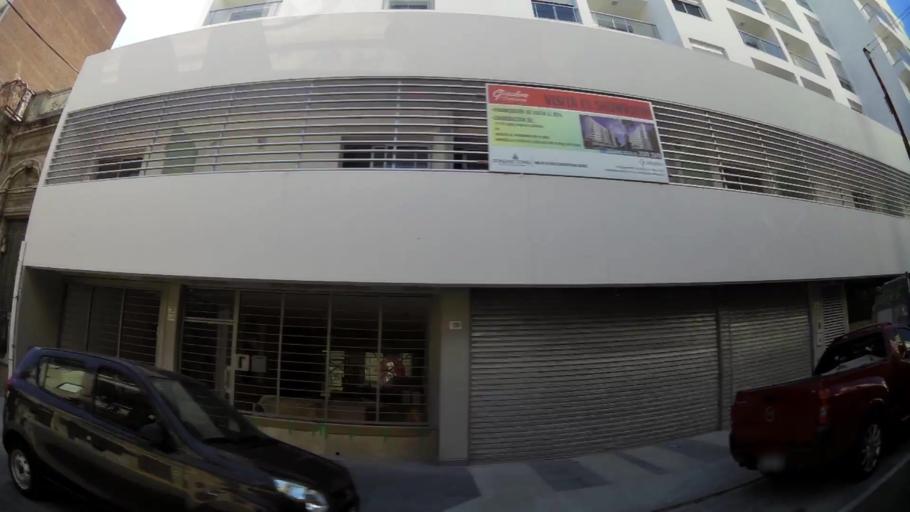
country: UY
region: Montevideo
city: Montevideo
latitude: -34.9061
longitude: -56.1785
